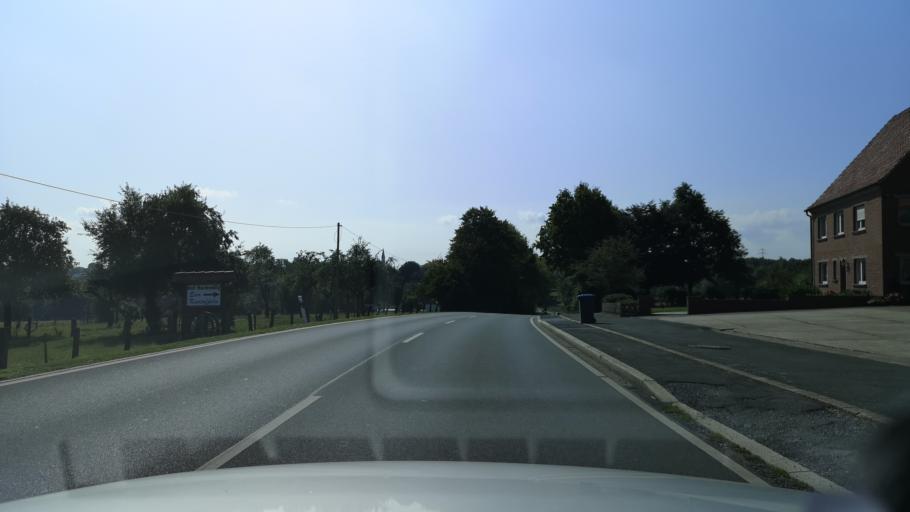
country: DE
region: North Rhine-Westphalia
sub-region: Regierungsbezirk Arnsberg
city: Frondenberg
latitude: 51.4960
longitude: 7.7732
